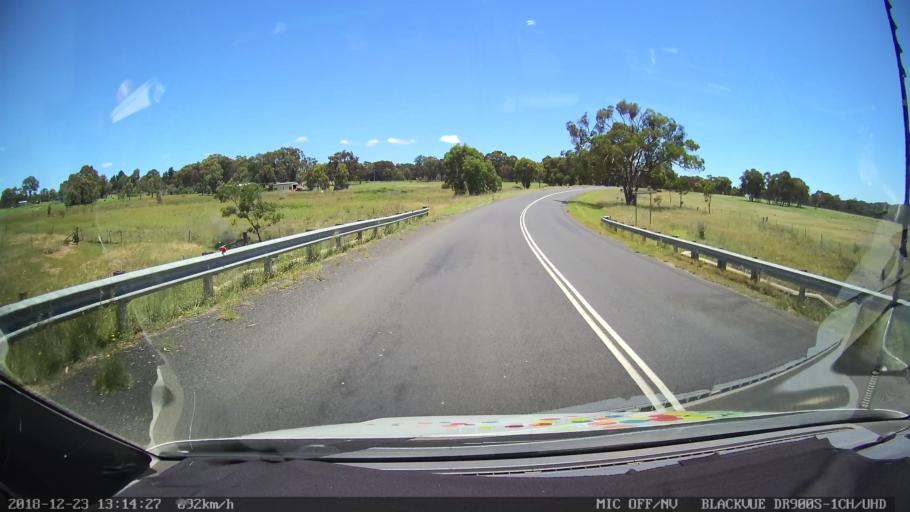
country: AU
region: New South Wales
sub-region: Armidale Dumaresq
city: Armidale
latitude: -30.5044
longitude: 151.5272
